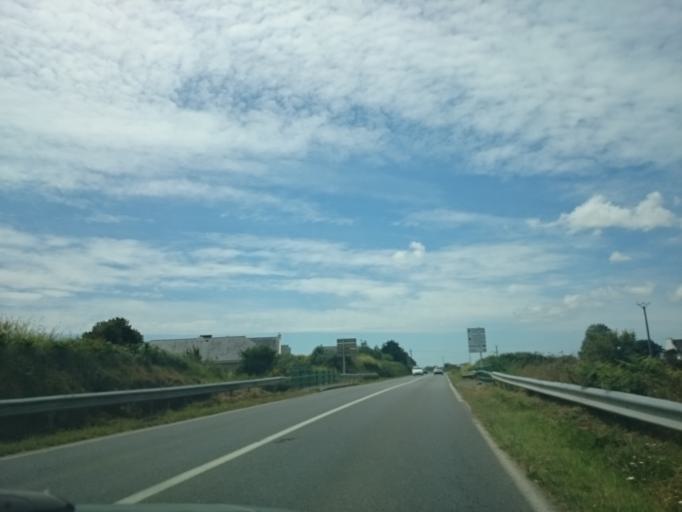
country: FR
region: Brittany
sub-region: Departement du Finistere
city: Plouzane
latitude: 48.3616
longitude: -4.6130
